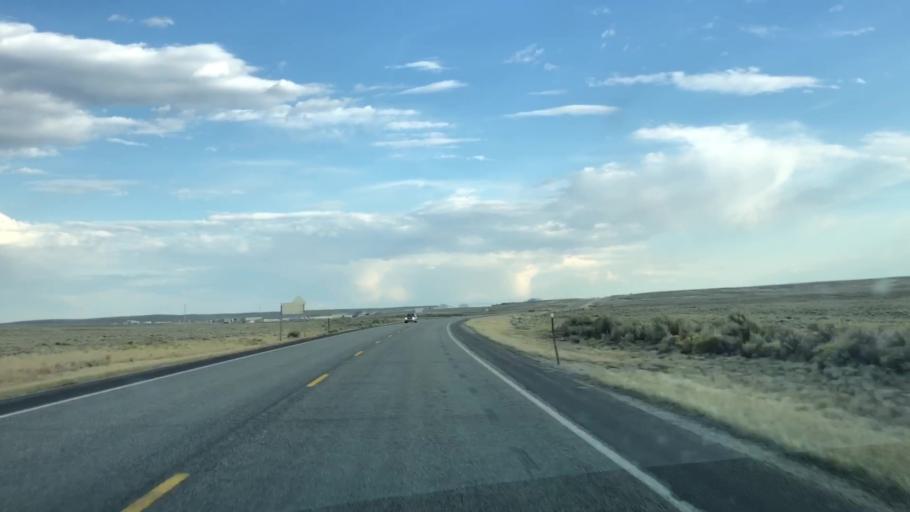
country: US
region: Wyoming
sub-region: Sublette County
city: Pinedale
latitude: 42.6195
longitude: -109.6507
